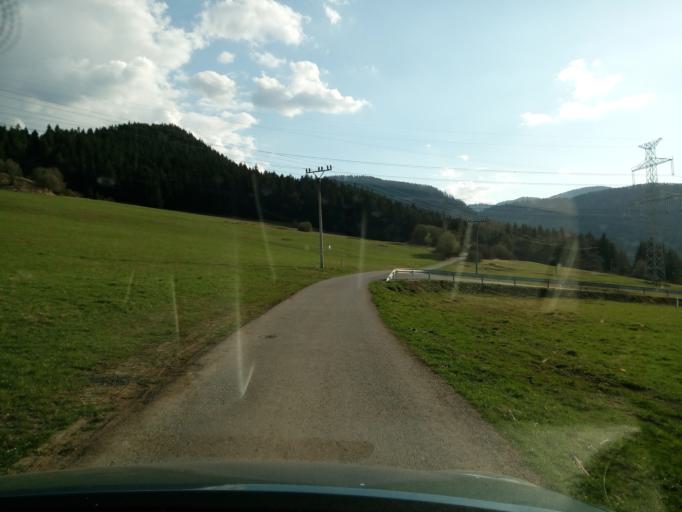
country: SK
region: Zilinsky
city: Ruzomberok
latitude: 49.0744
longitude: 19.2852
